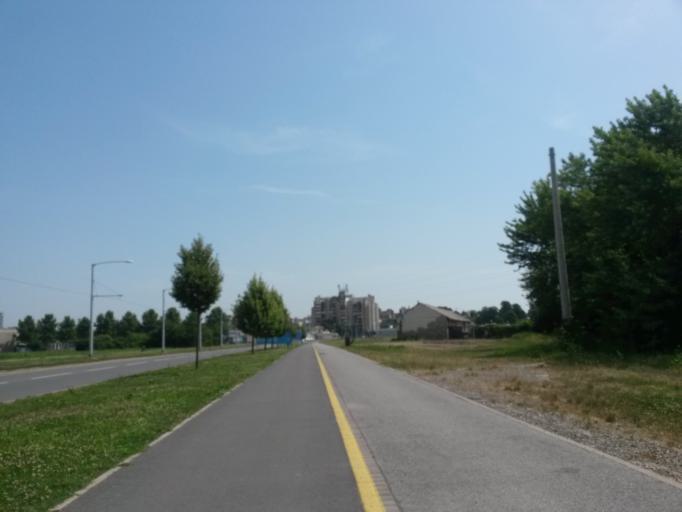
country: HR
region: Osjecko-Baranjska
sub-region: Grad Osijek
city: Osijek
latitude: 45.5474
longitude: 18.6889
